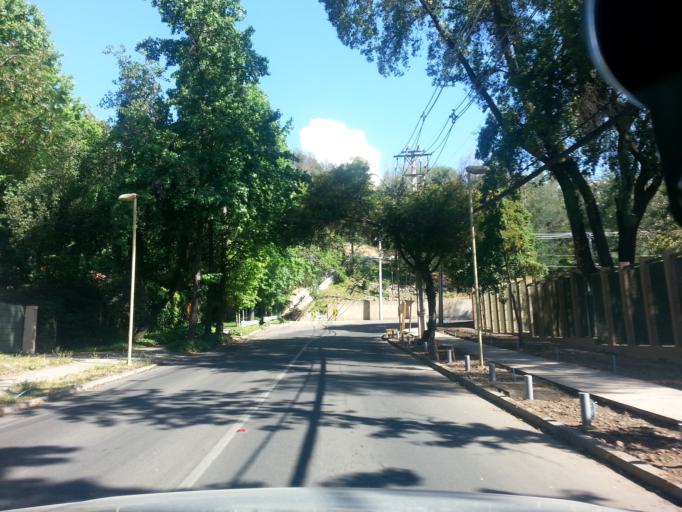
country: CL
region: Santiago Metropolitan
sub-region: Provincia de Santiago
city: Villa Presidente Frei, Nunoa, Santiago, Chile
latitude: -33.3846
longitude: -70.5197
